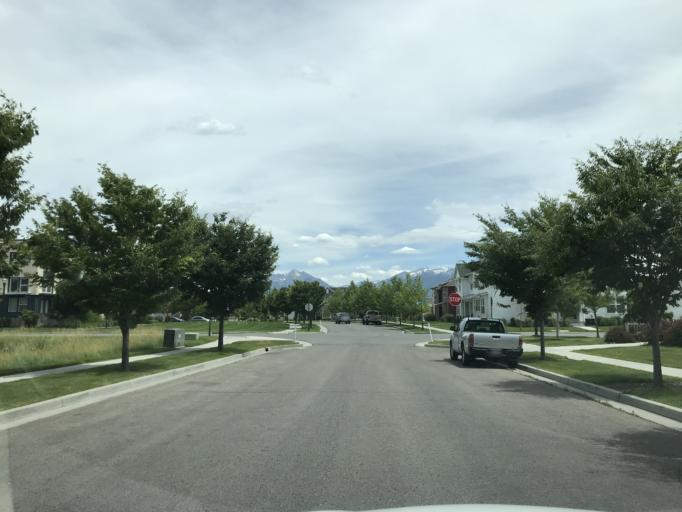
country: US
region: Utah
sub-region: Salt Lake County
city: South Jordan Heights
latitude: 40.5642
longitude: -112.0005
